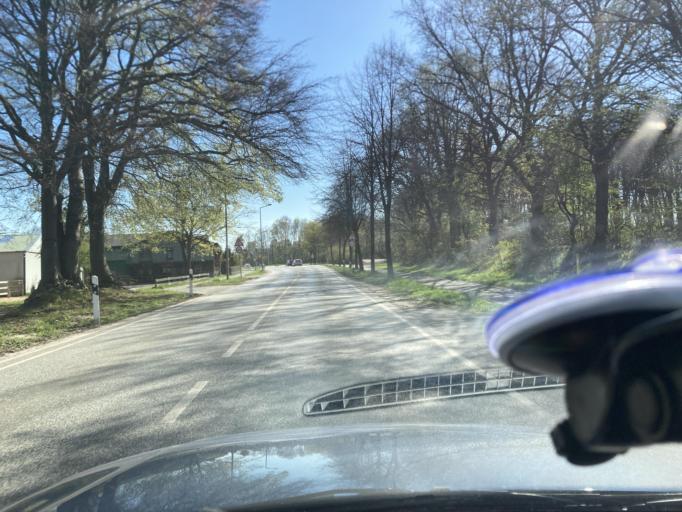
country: DE
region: Schleswig-Holstein
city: Ostrohe
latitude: 54.1973
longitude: 9.1388
